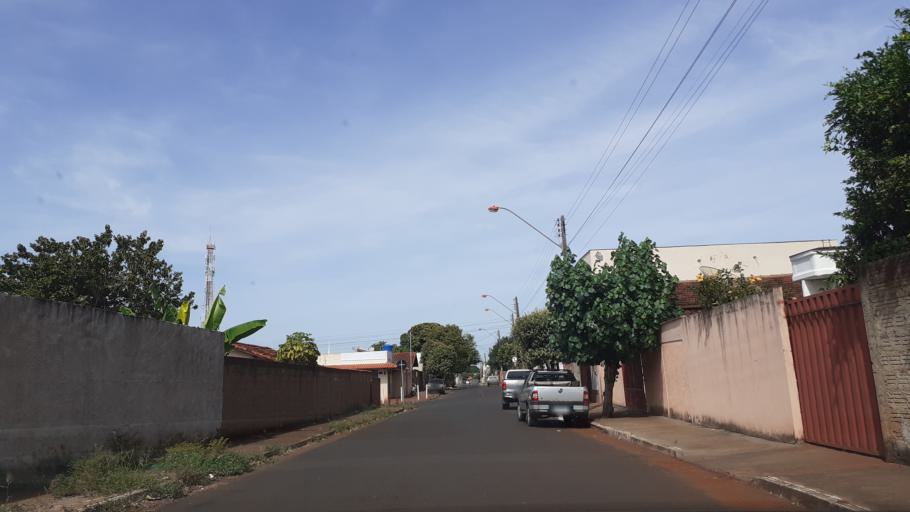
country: BR
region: Goias
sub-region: Itumbiara
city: Itumbiara
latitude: -18.4144
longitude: -49.2298
